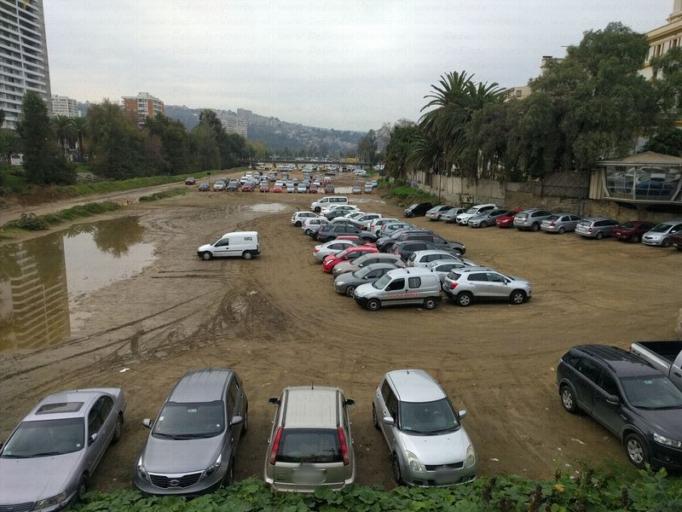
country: CL
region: Valparaiso
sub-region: Provincia de Valparaiso
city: Vina del Mar
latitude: -33.0233
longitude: -71.5515
